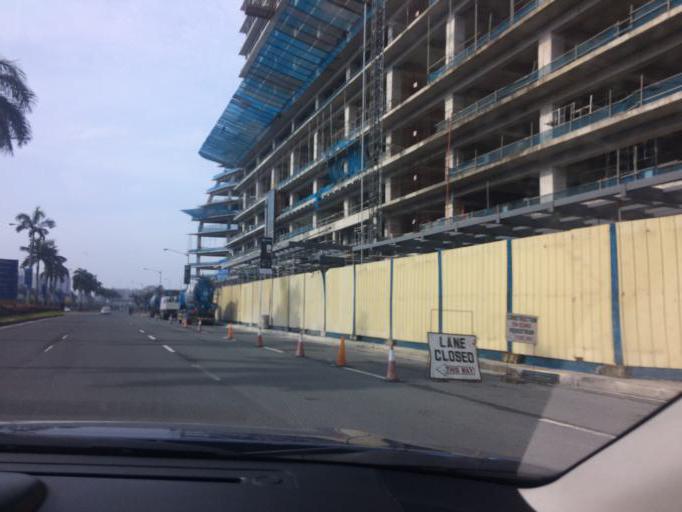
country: PH
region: Metro Manila
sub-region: City of Manila
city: Port Area
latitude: 14.5418
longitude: 120.9831
